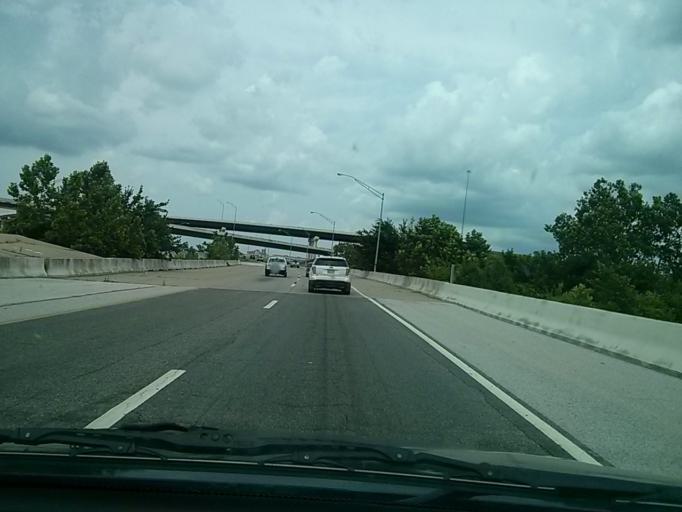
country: US
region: Oklahoma
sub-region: Tulsa County
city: Broken Arrow
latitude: 36.0274
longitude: -95.8642
